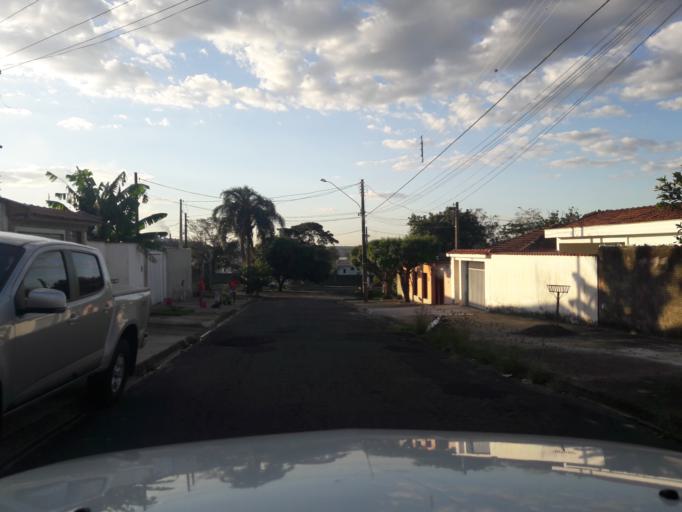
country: BR
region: Sao Paulo
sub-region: Moji-Guacu
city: Mogi-Gaucu
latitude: -22.3941
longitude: -46.9492
